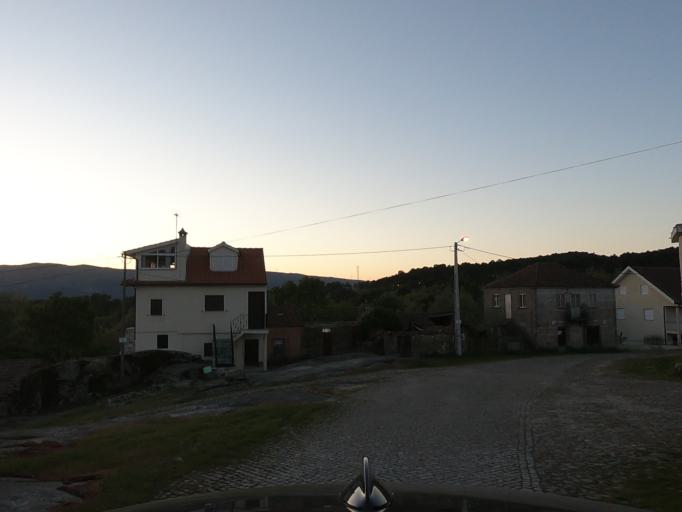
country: PT
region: Vila Real
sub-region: Vila Real
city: Vila Real
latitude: 41.3122
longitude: -7.6718
